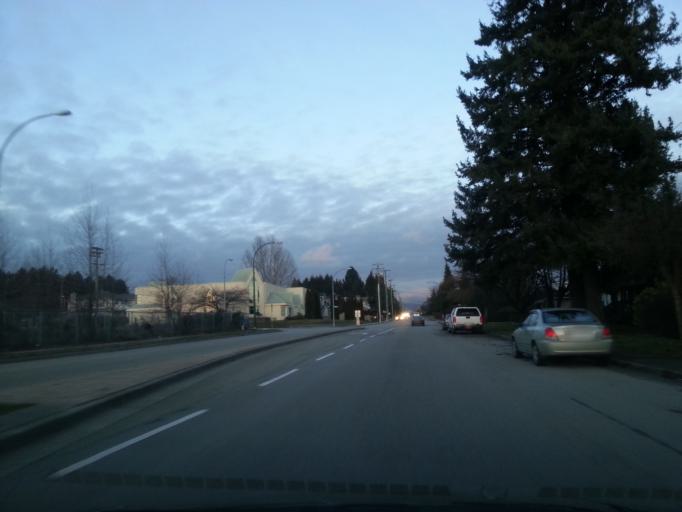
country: CA
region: British Columbia
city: New Westminster
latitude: 49.2074
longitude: -122.9490
